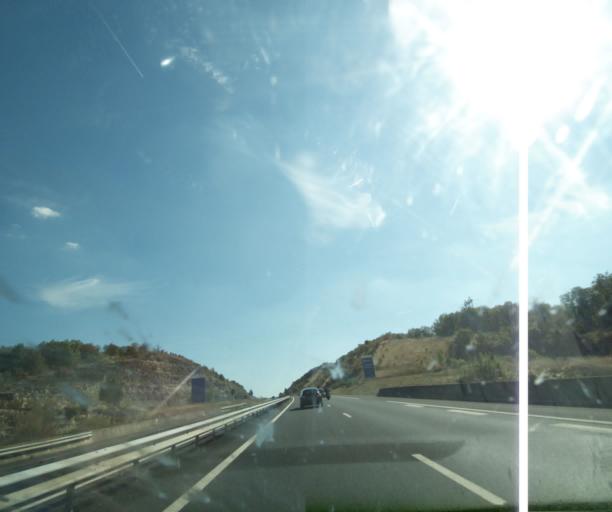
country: FR
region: Limousin
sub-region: Departement de la Correze
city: Brive-la-Gaillarde
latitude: 45.0595
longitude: 1.5068
